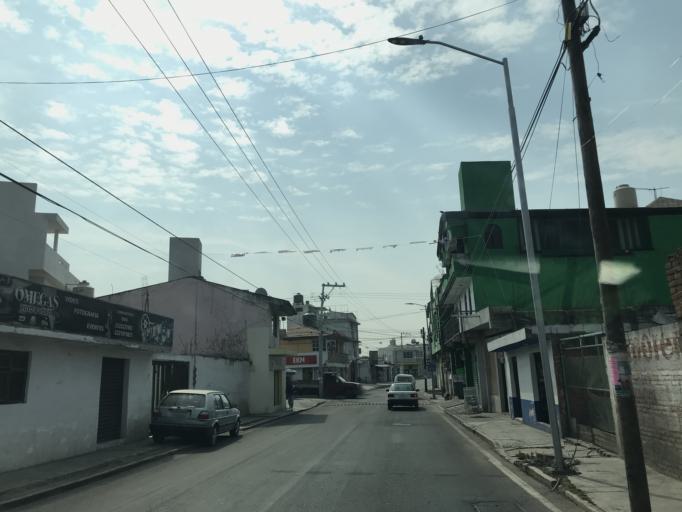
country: MX
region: Tlaxcala
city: Tenancingo
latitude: 19.1471
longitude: -98.1998
